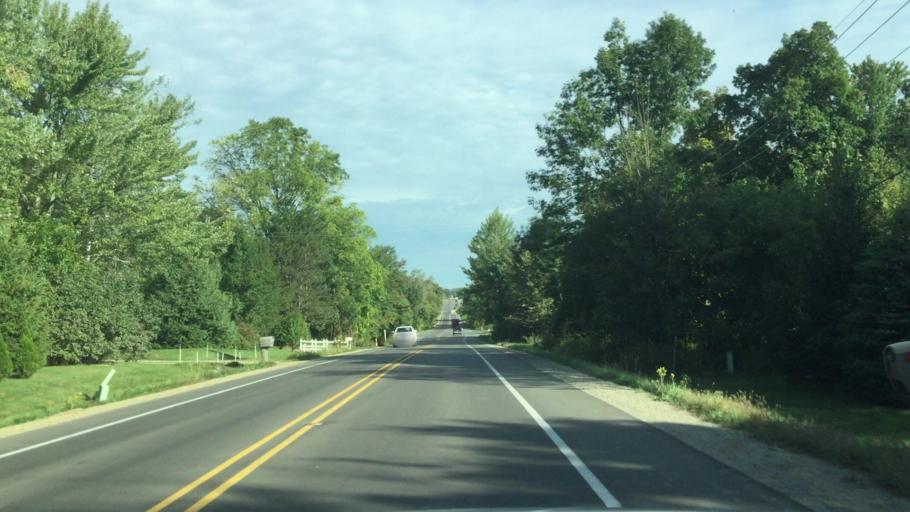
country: US
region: Michigan
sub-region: Livingston County
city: Howell
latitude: 42.6160
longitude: -83.8750
